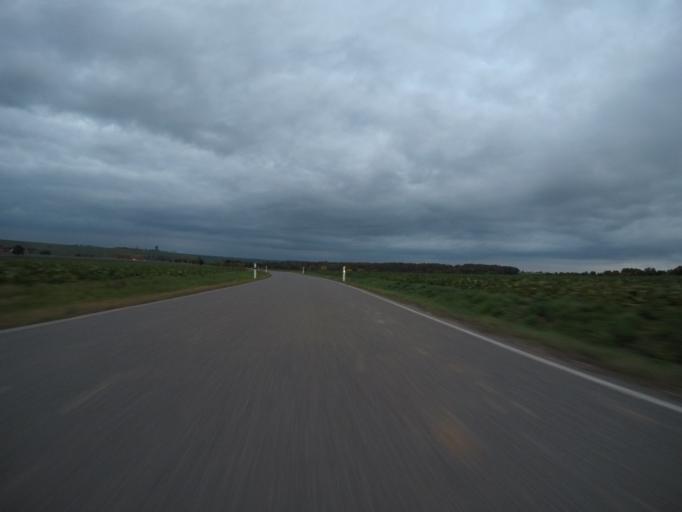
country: DE
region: Thuringia
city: Saara
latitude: 50.9143
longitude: 12.4017
